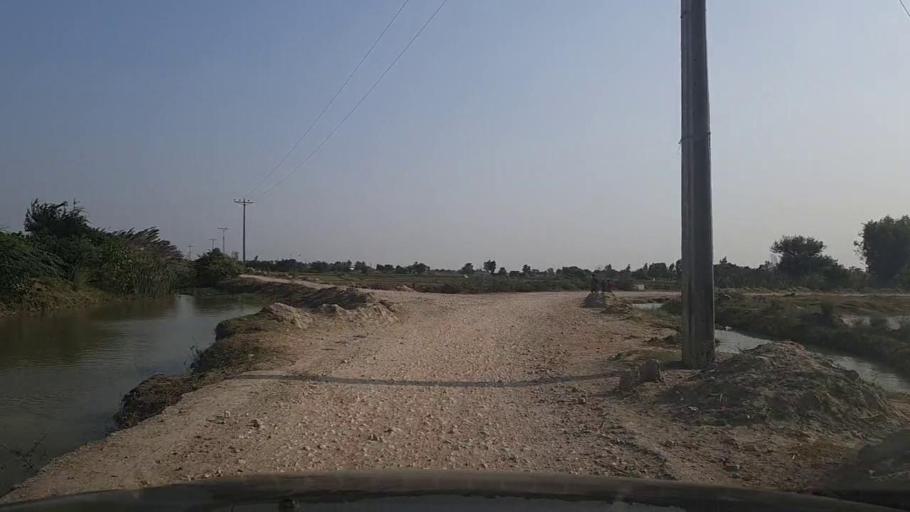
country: PK
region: Sindh
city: Mirpur Sakro
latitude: 24.6288
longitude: 67.7562
